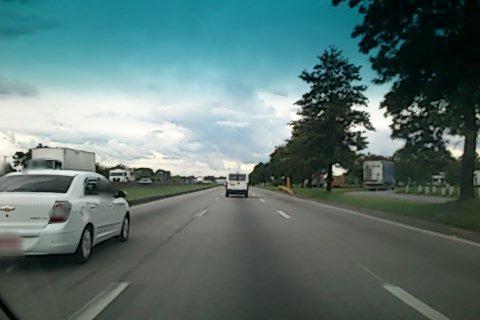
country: BR
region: Sao Paulo
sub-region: Sao Jose Dos Campos
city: Sao Jose dos Campos
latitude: -23.2399
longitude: -45.9217
